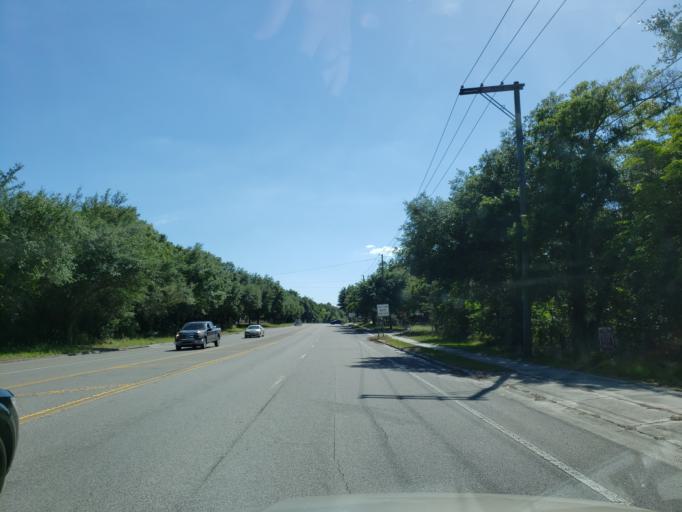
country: US
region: Florida
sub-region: Hillsborough County
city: Mango
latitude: 27.9763
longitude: -82.3119
